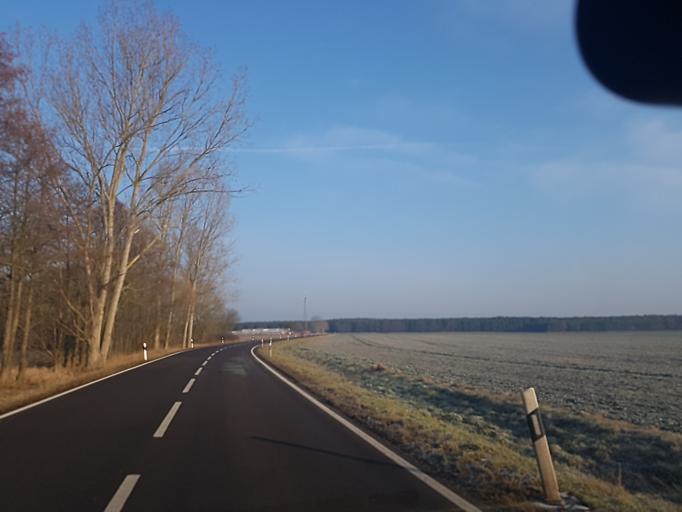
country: DE
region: Brandenburg
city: Bruck
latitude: 52.2048
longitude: 12.7515
